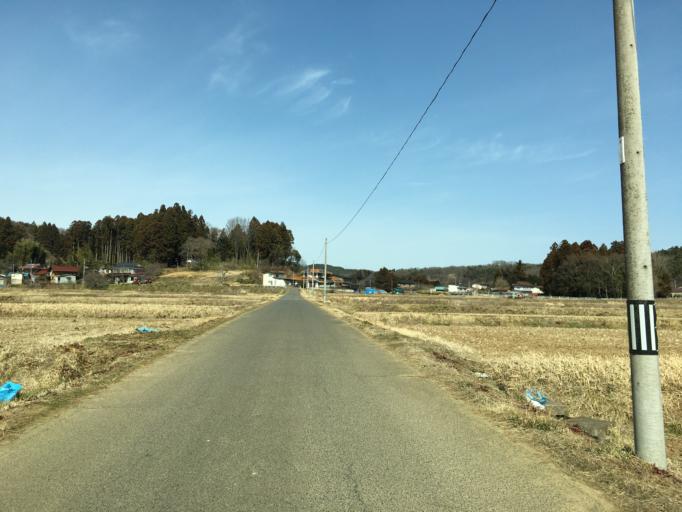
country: JP
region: Fukushima
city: Nihommatsu
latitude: 37.5875
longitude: 140.3867
